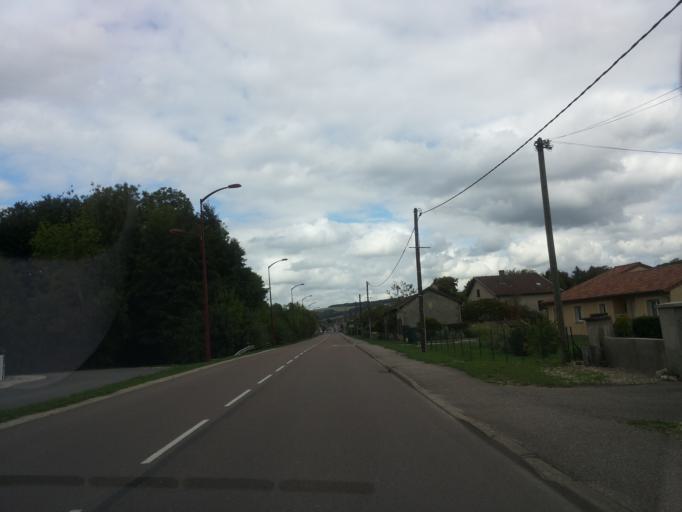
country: FR
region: Lorraine
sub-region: Departement de la Meuse
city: Ligny-en-Barrois
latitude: 48.6779
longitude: 5.3256
